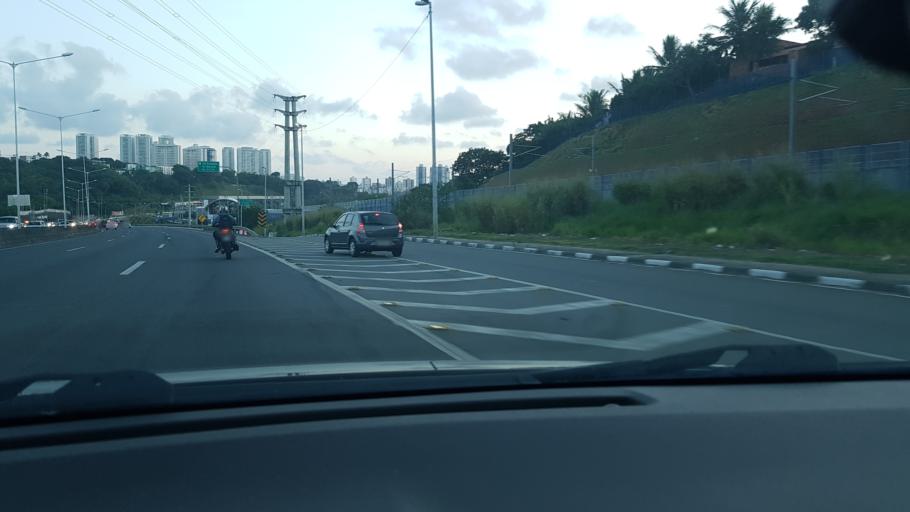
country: BR
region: Bahia
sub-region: Salvador
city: Salvador
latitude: -12.9516
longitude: -38.4712
